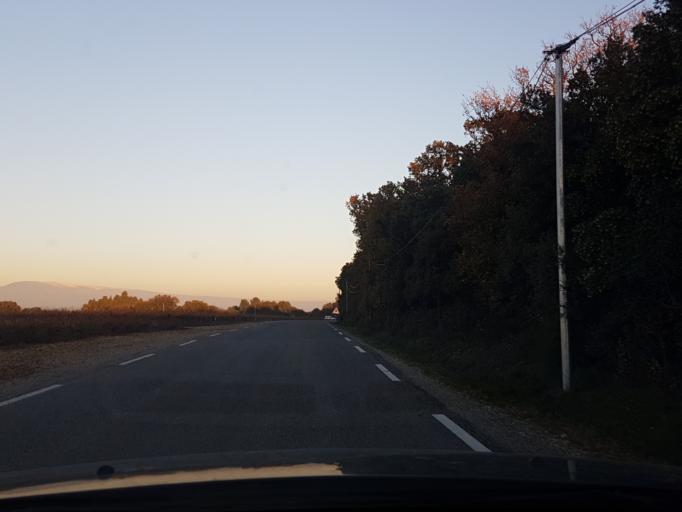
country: FR
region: Provence-Alpes-Cote d'Azur
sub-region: Departement du Vaucluse
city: Saint-Saturnin-les-Avignon
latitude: 43.9460
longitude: 4.9223
